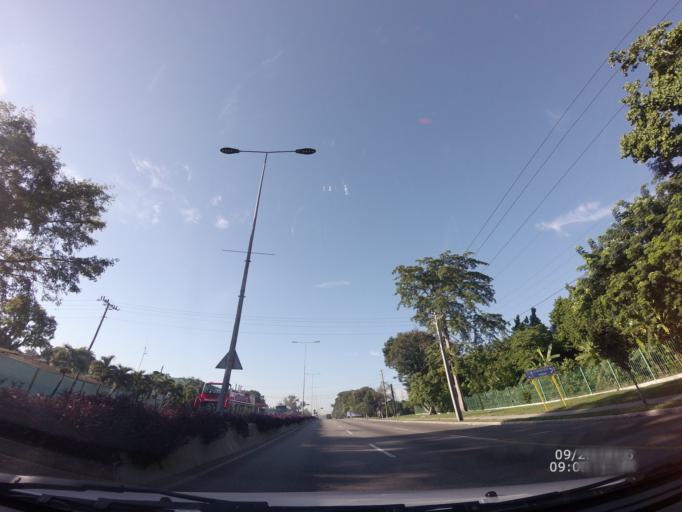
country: CU
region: La Habana
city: Arroyo Naranjo
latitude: 23.0540
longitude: -82.4035
